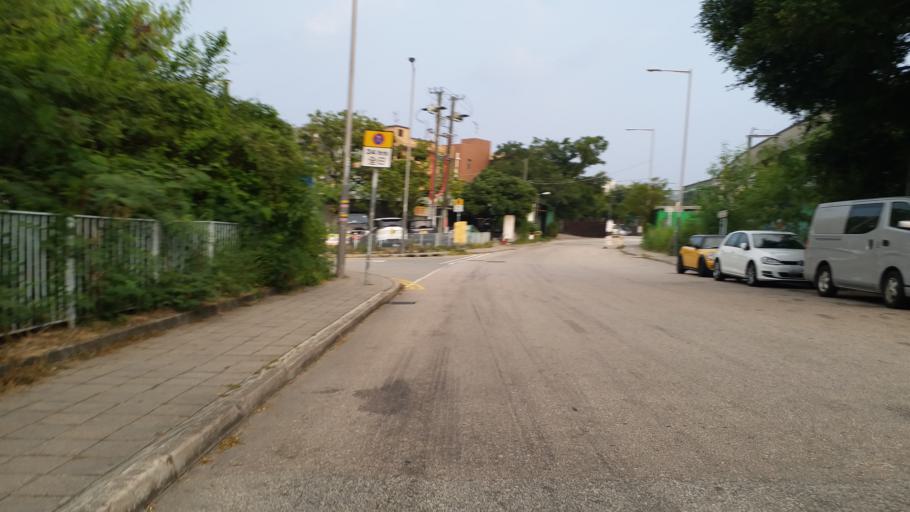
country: HK
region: Yuen Long
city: Yuen Long Kau Hui
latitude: 22.4518
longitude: 114.0102
